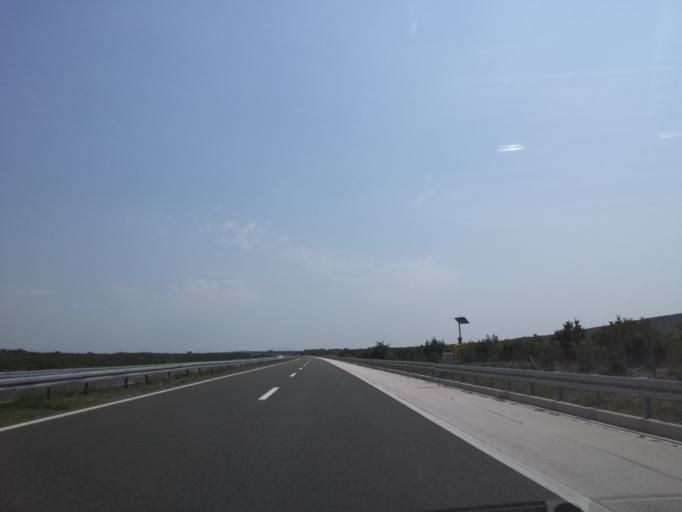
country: HR
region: Sibensko-Kniniska
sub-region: Grad Sibenik
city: Pirovac
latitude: 43.9390
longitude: 15.7031
